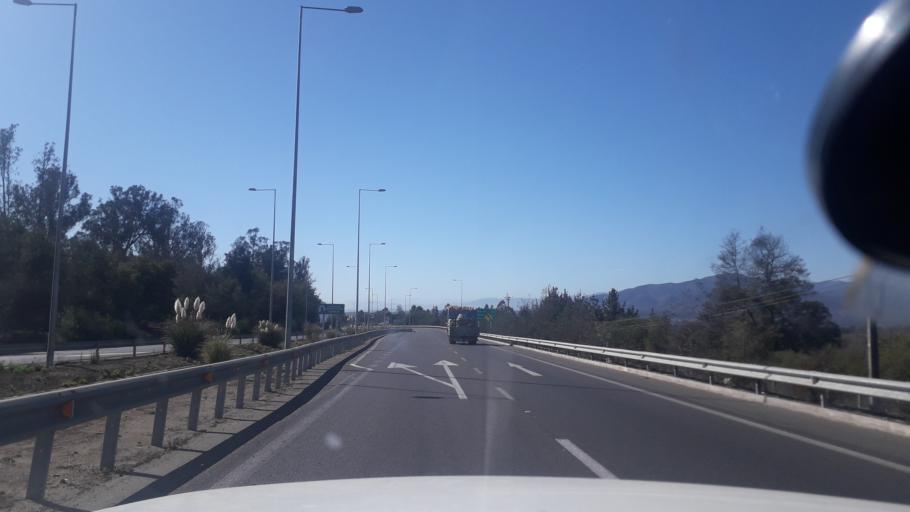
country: CL
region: Valparaiso
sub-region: Provincia de Valparaiso
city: Vina del Mar
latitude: -32.9563
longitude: -71.5100
